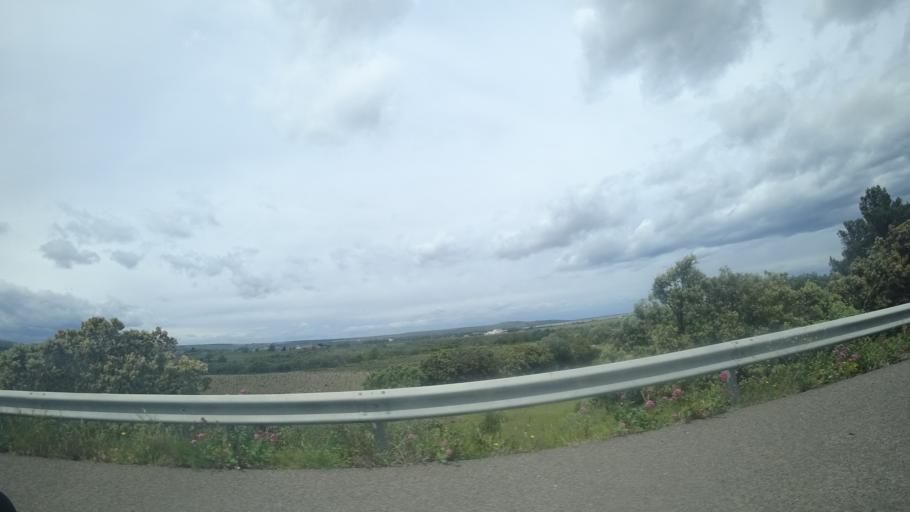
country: FR
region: Languedoc-Roussillon
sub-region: Departement de l'Aude
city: Leucate
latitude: 42.9378
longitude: 2.9853
